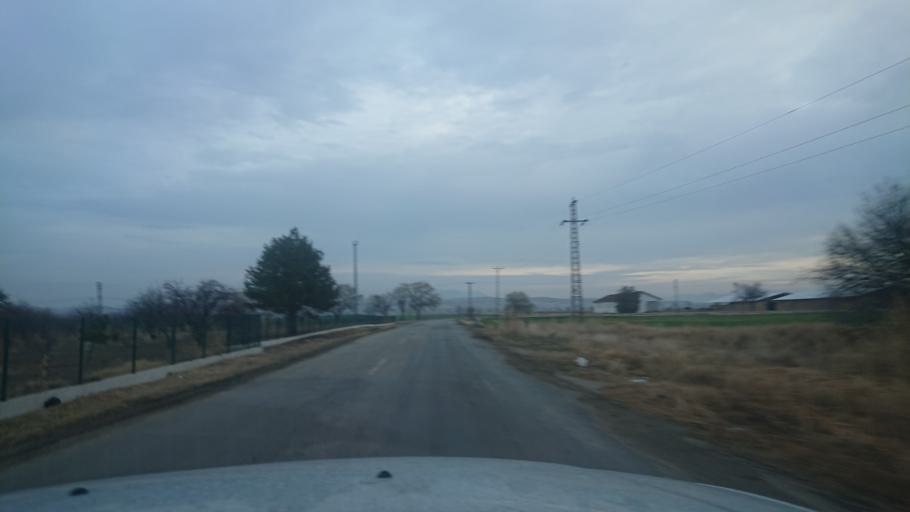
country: TR
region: Aksaray
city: Yesilova
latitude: 38.4585
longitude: 33.8424
